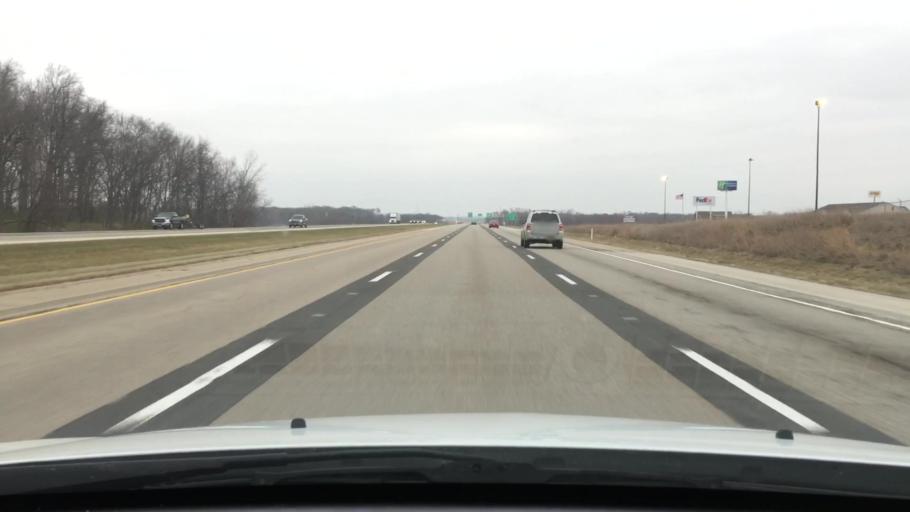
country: US
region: Illinois
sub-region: Logan County
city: Lincoln
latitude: 40.1544
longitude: -89.4173
